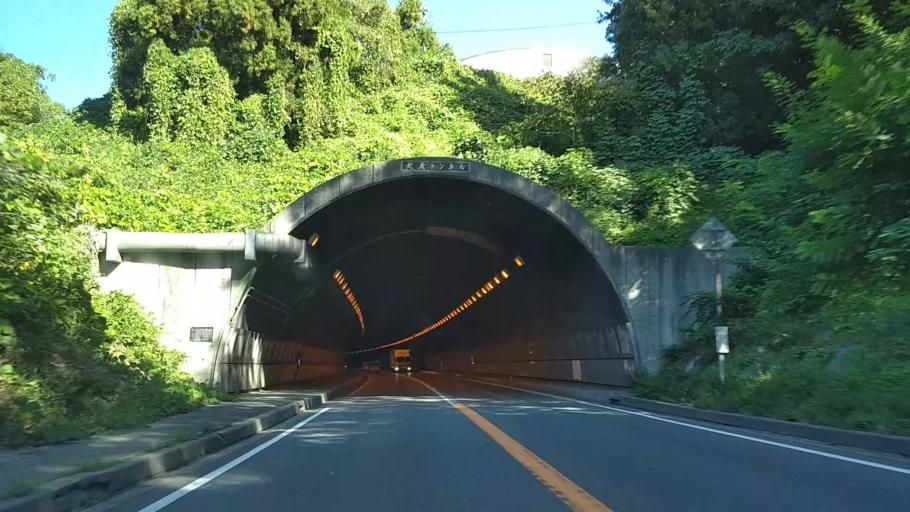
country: JP
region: Nagano
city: Nagano-shi
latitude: 36.6201
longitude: 138.1106
